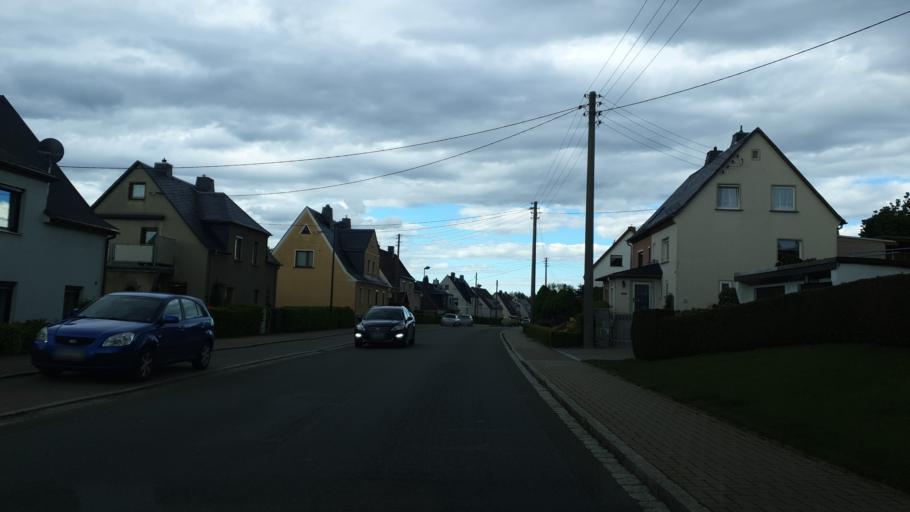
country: DE
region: Saxony
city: Gersdorf
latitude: 50.7357
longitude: 12.7135
